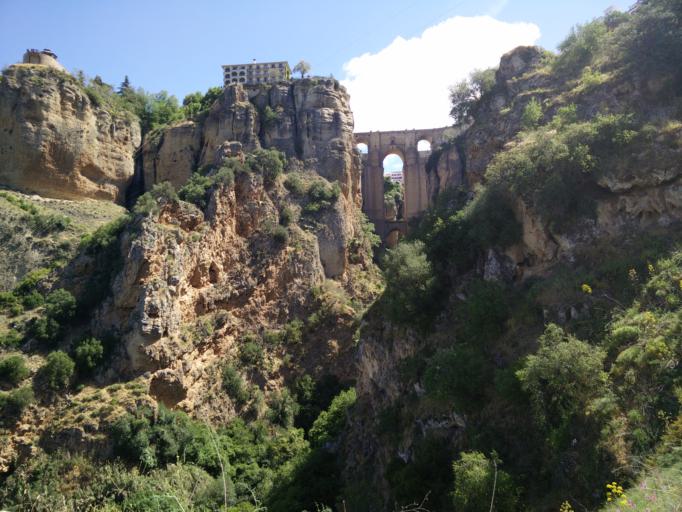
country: ES
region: Andalusia
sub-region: Provincia de Malaga
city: Ronda
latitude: 36.7392
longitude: -5.1692
